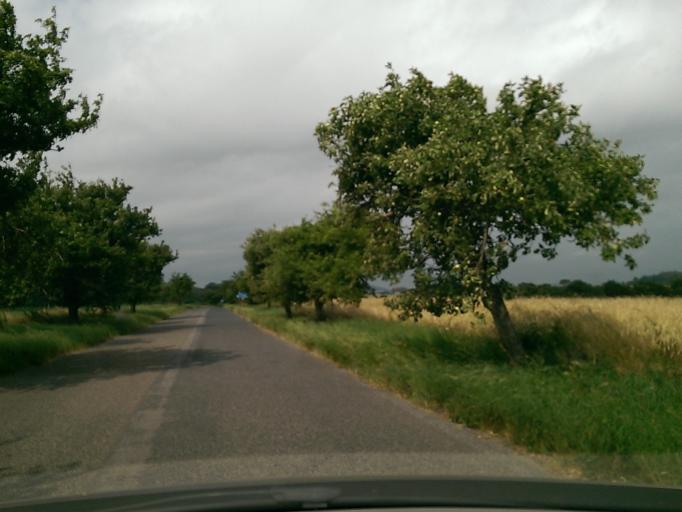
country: CZ
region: Central Bohemia
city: Bela pod Bezdezem
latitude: 50.4738
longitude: 14.7572
